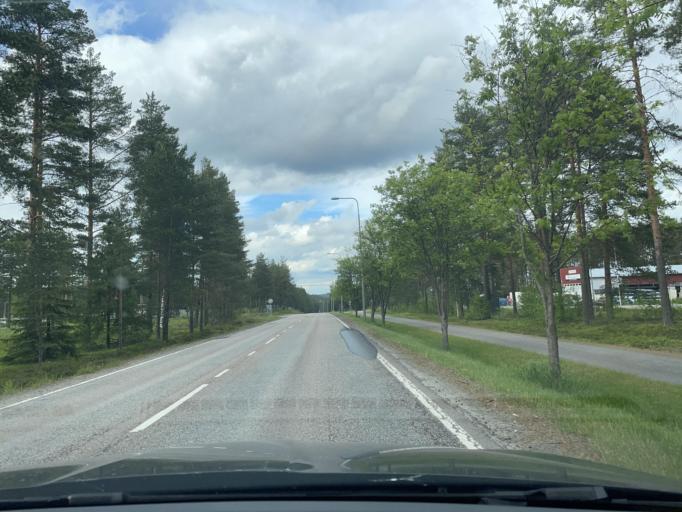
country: FI
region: Central Finland
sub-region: Jaemsae
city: Jaemsaenkoski
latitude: 61.9131
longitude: 25.1440
